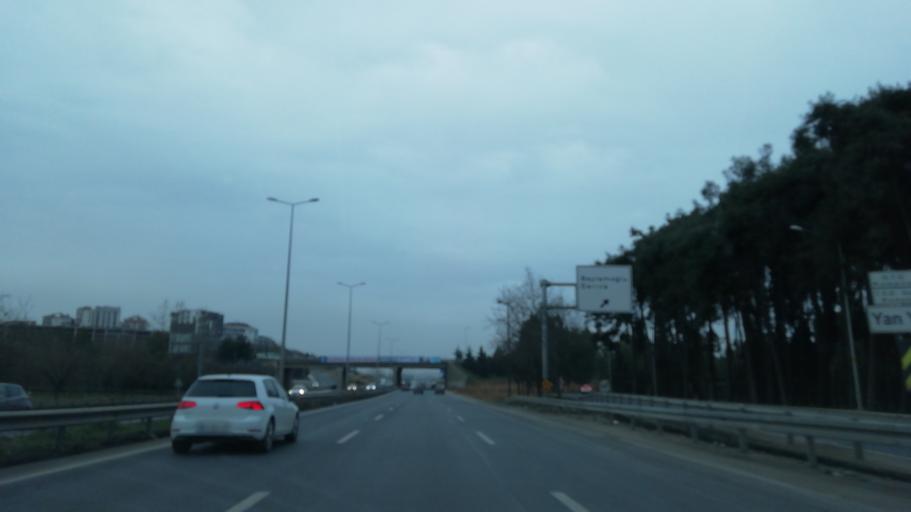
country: TR
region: Kocaeli
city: Darica
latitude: 40.8162
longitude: 29.3625
